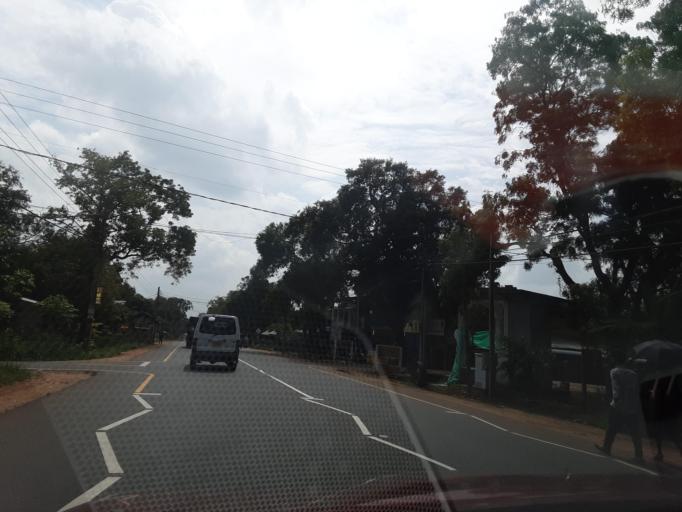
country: LK
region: North Central
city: Anuradhapura
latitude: 8.4895
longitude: 80.5112
